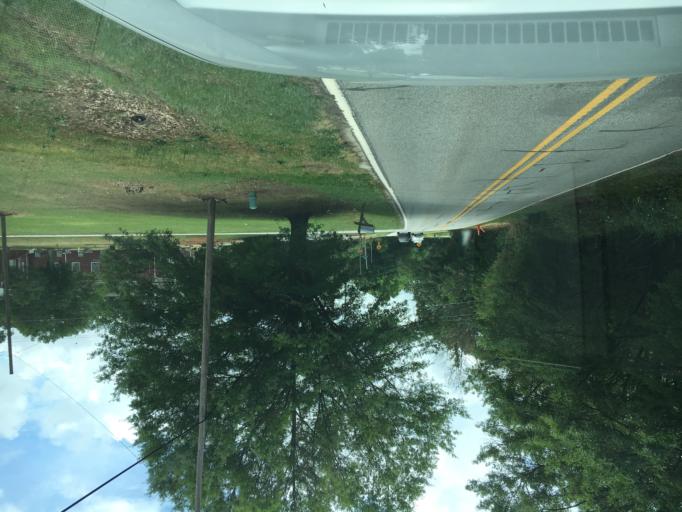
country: US
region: South Carolina
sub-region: Greenville County
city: Five Forks
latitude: 34.8410
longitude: -82.2799
